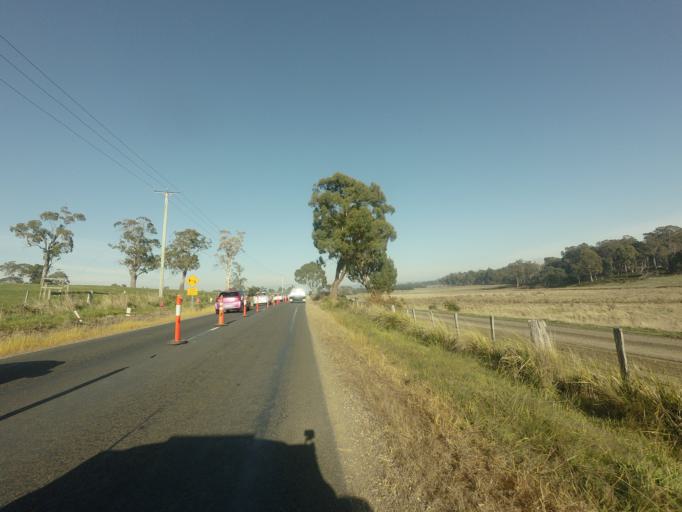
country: AU
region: Tasmania
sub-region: Northern Midlands
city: Longford
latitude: -41.5582
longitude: 146.9858
